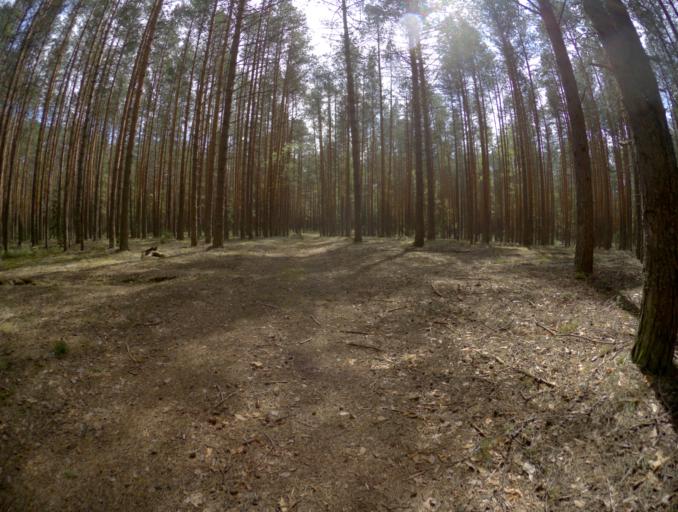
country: RU
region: Vladimir
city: Golovino
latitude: 55.9120
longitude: 40.3957
